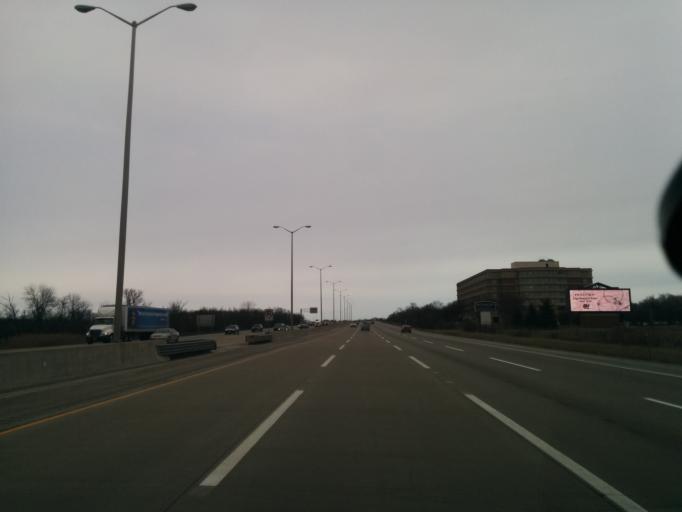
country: US
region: Illinois
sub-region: Cook County
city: Des Plaines
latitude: 42.0772
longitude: -87.8664
